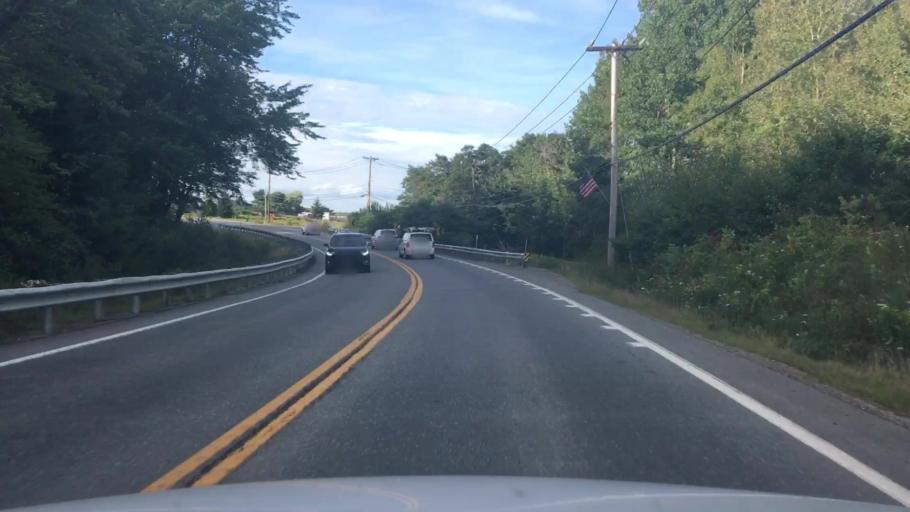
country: US
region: Maine
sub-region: Hancock County
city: Trenton
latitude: 44.4816
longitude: -68.3657
